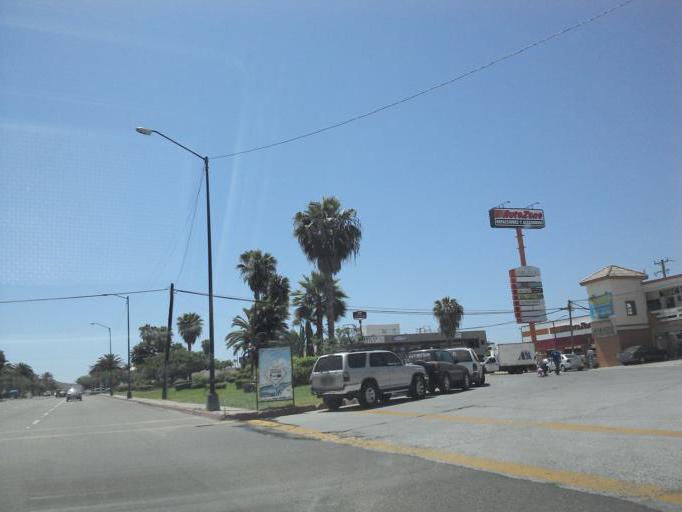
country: US
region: California
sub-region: San Diego County
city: Imperial Beach
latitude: 32.5281
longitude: -117.1162
